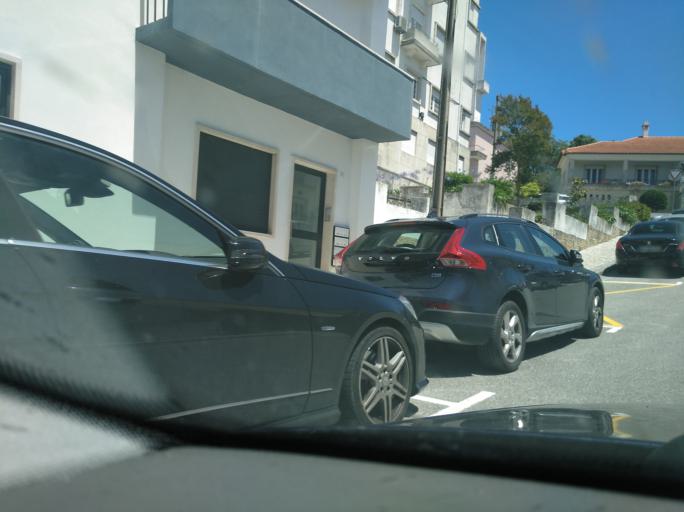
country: PT
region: Coimbra
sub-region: Coimbra
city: Coimbra
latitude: 40.2118
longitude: -8.4198
